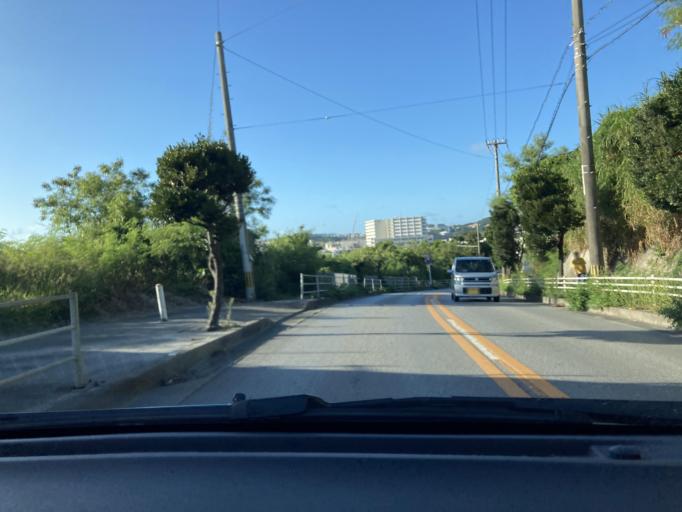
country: JP
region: Okinawa
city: Tomigusuku
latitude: 26.1862
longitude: 127.7301
